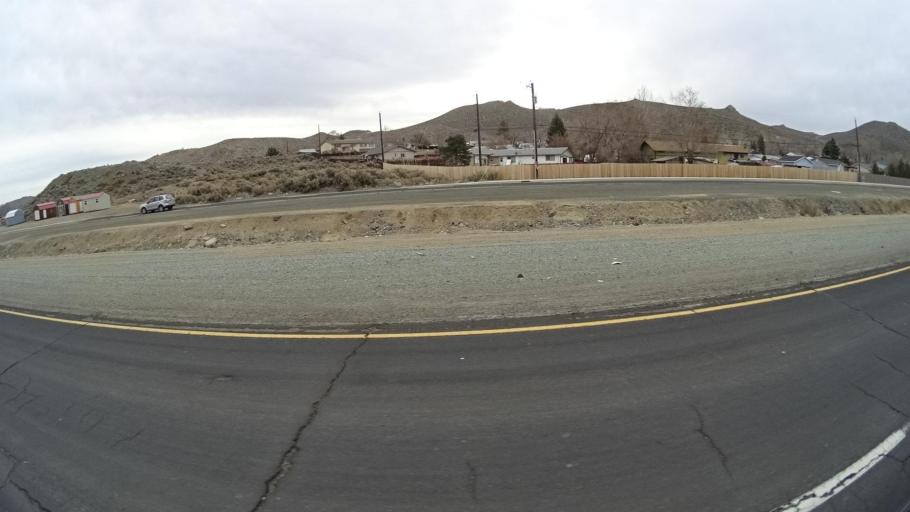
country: US
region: Nevada
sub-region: Washoe County
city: Lemmon Valley
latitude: 39.6341
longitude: -119.8449
